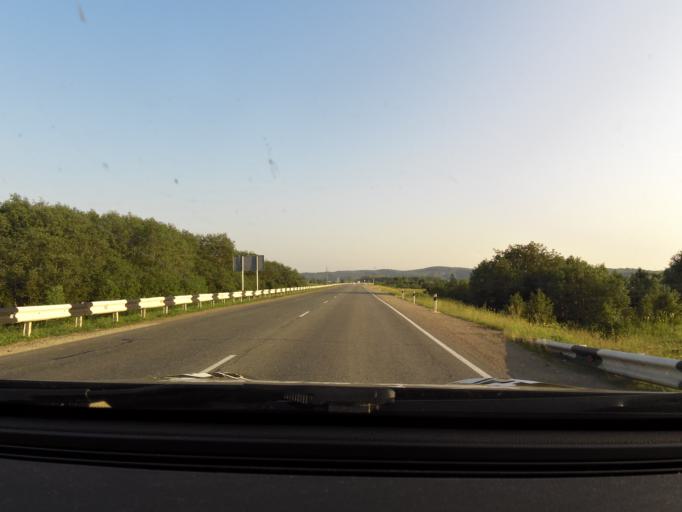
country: RU
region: Sverdlovsk
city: Mikhaylovsk
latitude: 56.4371
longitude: 59.0856
